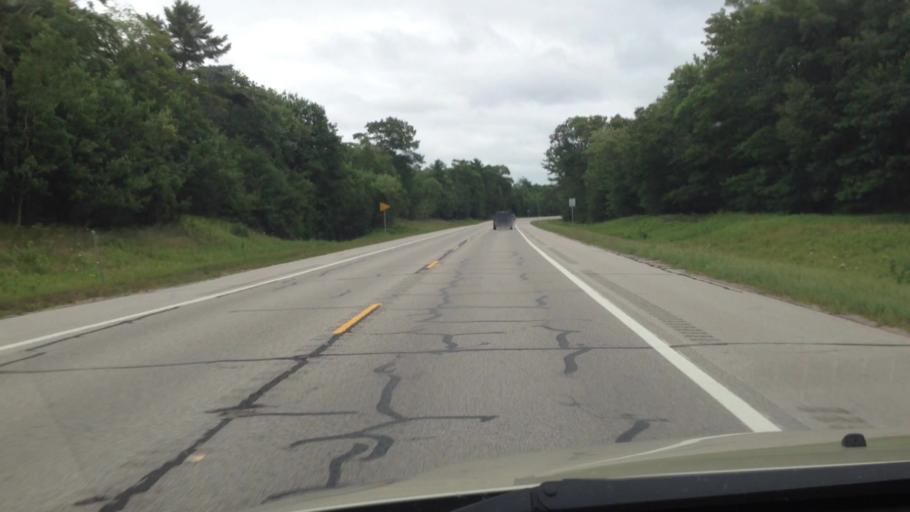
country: US
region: Michigan
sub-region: Mackinac County
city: Saint Ignace
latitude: 46.0080
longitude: -85.0044
